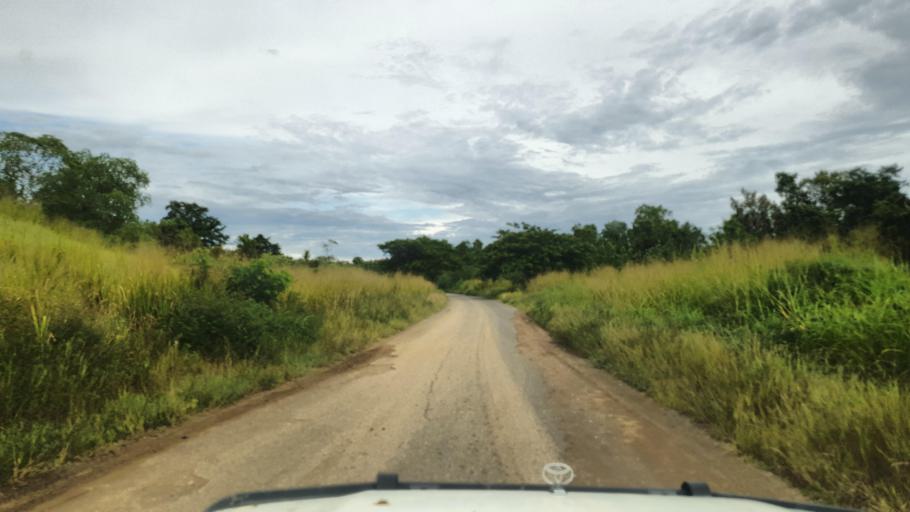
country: PG
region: Gulf
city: Kerema
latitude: -8.3348
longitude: 146.3189
